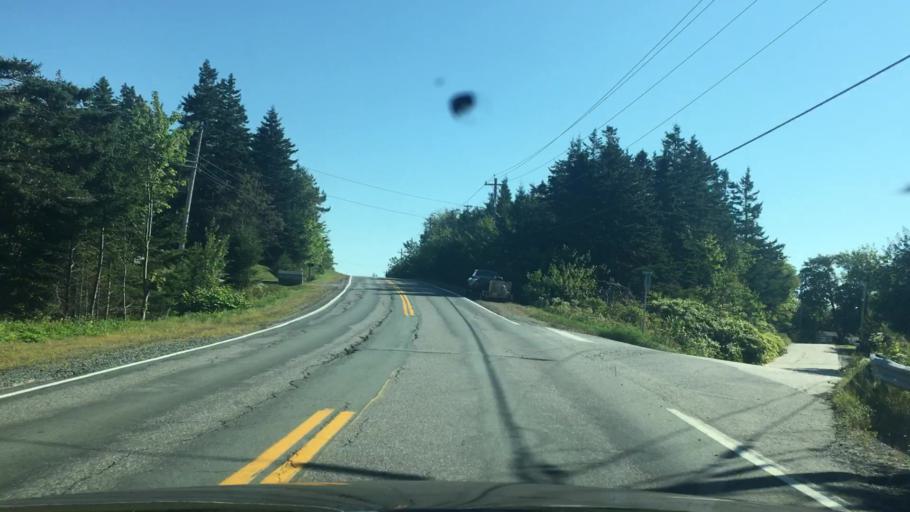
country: CA
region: Nova Scotia
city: Cole Harbour
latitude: 44.7767
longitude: -63.0674
